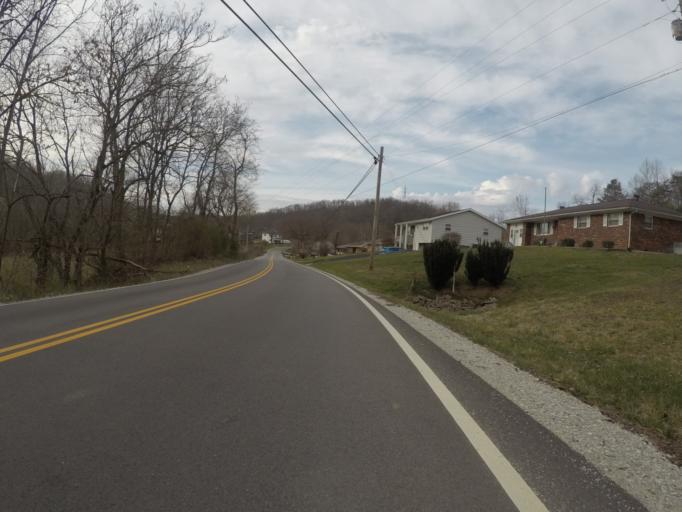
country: US
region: Ohio
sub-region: Lawrence County
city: Burlington
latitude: 38.4451
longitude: -82.5027
